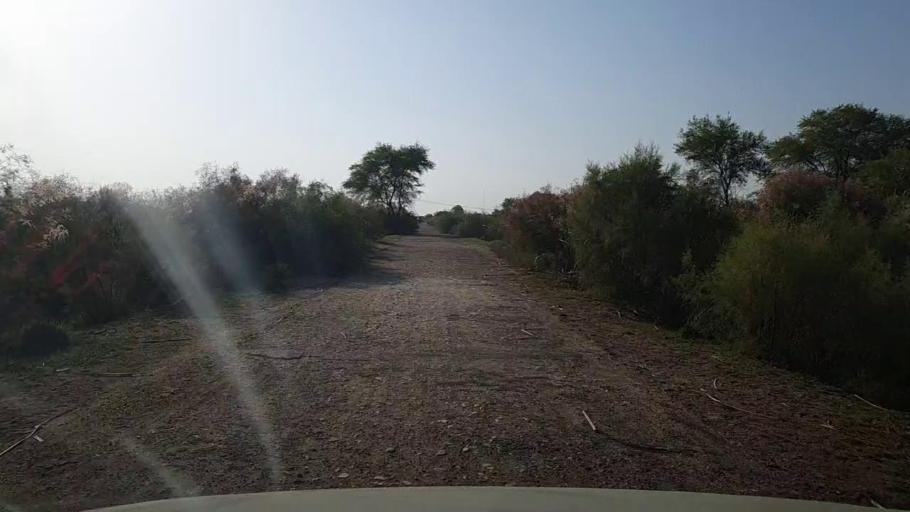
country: PK
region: Sindh
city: Kandhkot
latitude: 28.2898
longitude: 69.3264
